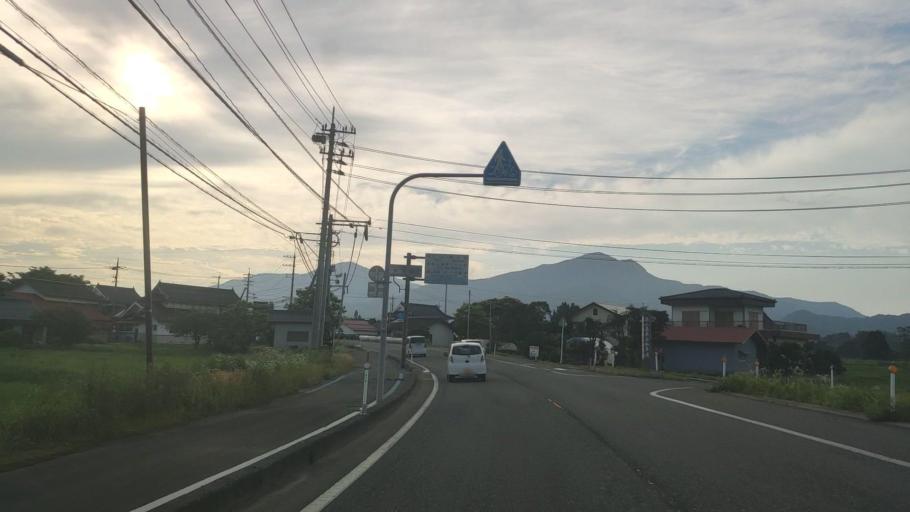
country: JP
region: Tottori
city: Kurayoshi
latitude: 35.2910
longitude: 133.7328
